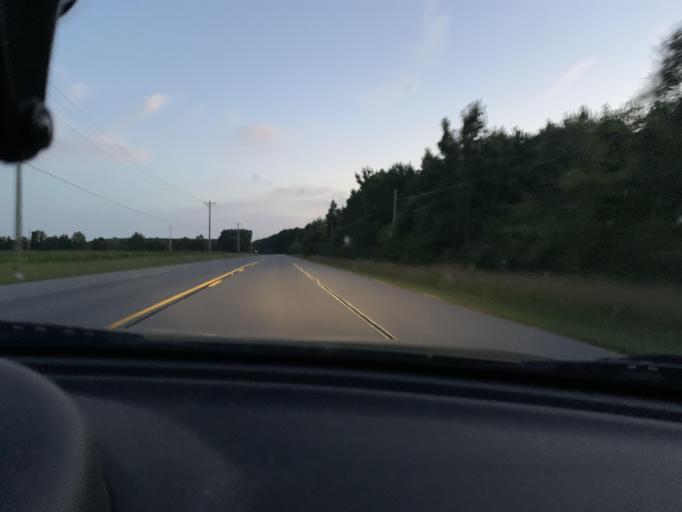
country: US
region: Maryland
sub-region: Talbot County
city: Saint Michaels
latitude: 38.7519
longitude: -76.3221
